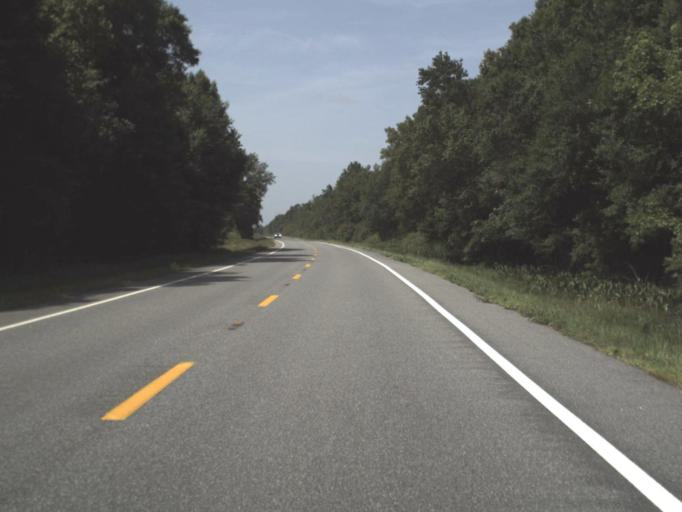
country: US
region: Florida
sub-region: Lafayette County
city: Mayo
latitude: 29.8780
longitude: -83.3063
